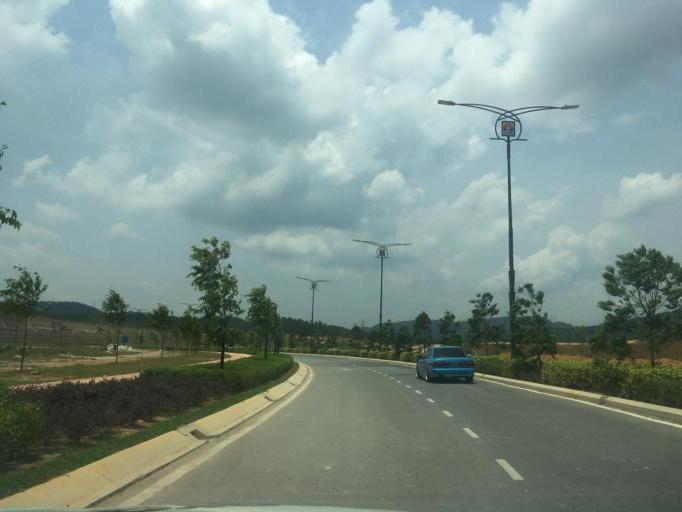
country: MY
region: Putrajaya
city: Putrajaya
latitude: 2.8452
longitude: 101.7046
